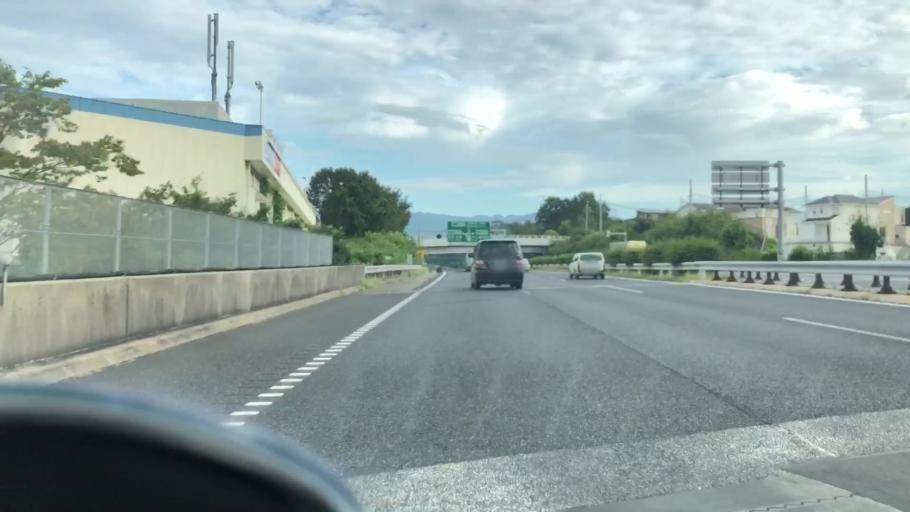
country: JP
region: Hyogo
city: Sandacho
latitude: 34.8580
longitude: 135.2162
